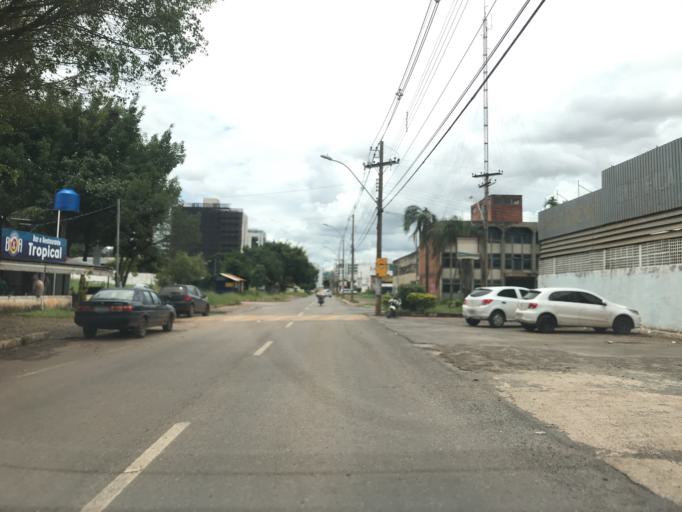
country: BR
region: Federal District
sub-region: Brasilia
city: Brasilia
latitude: -15.8245
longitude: -47.9566
